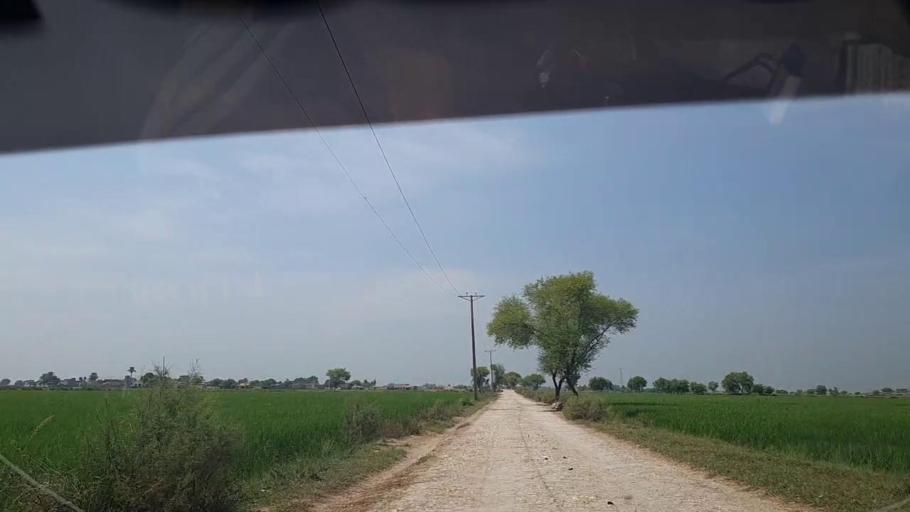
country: PK
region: Sindh
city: Thul
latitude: 28.1735
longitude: 68.7452
